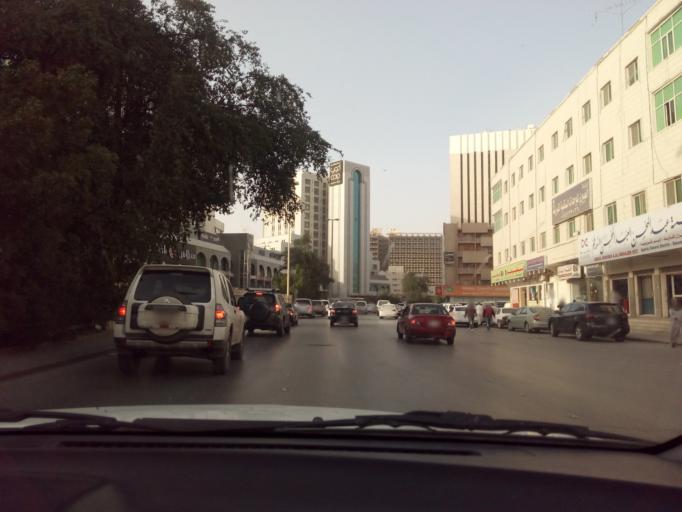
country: SA
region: Ar Riyad
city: Riyadh
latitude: 24.6320
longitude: 46.7165
